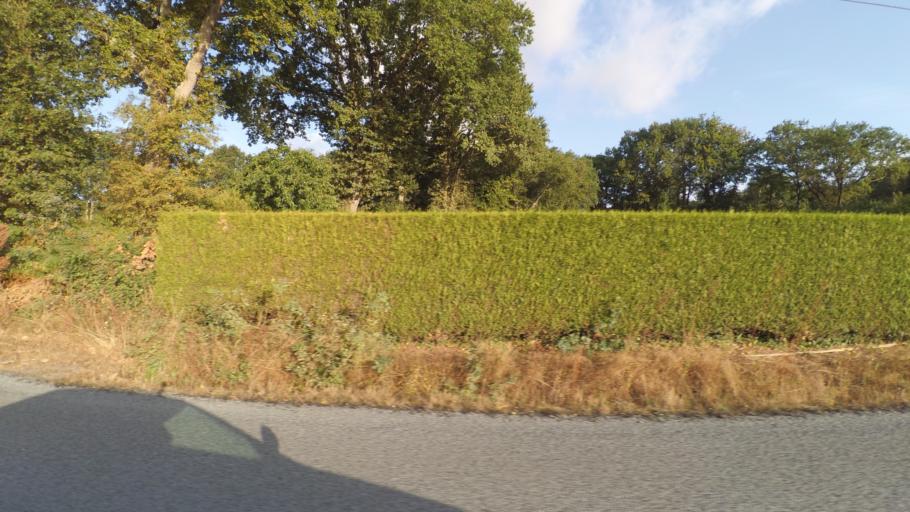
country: FR
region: Pays de la Loire
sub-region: Departement de la Loire-Atlantique
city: La Planche
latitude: 47.0116
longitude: -1.4450
